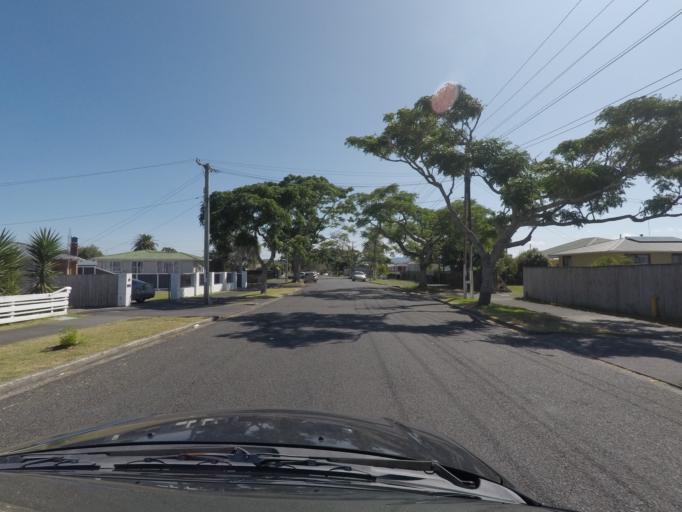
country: NZ
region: Auckland
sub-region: Auckland
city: Rosebank
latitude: -36.8960
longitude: 174.6831
